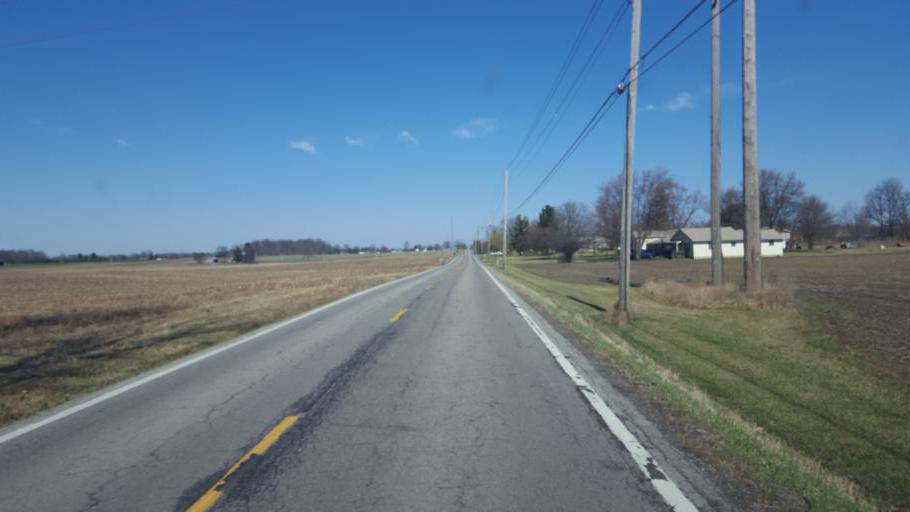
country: US
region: Ohio
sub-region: Marion County
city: Prospect
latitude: 40.5153
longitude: -83.1899
